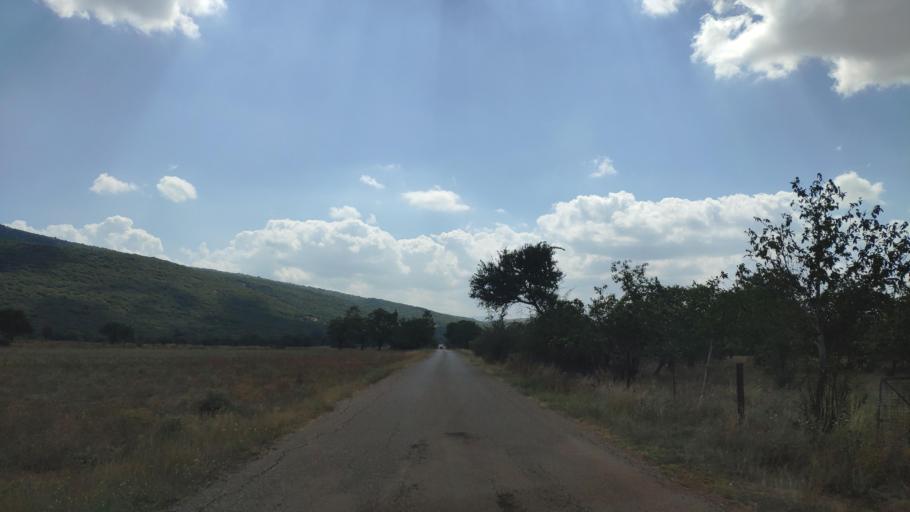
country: GR
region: Peloponnese
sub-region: Nomos Lakonias
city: Kariai
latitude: 37.3157
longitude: 22.4426
